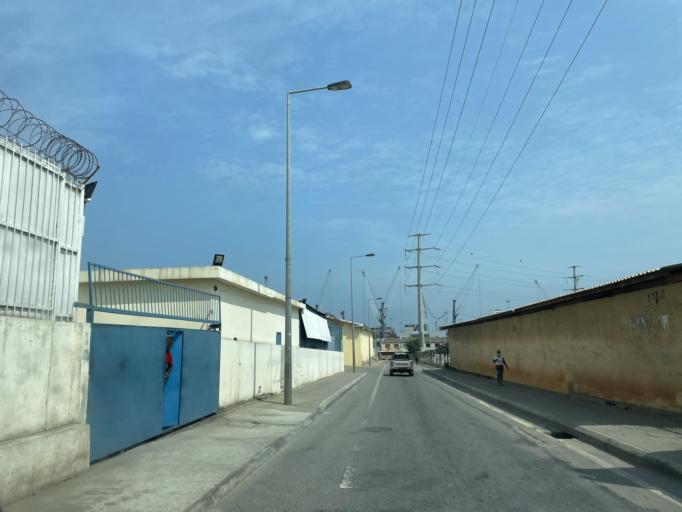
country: AO
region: Luanda
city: Luanda
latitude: -8.8049
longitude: 13.2529
